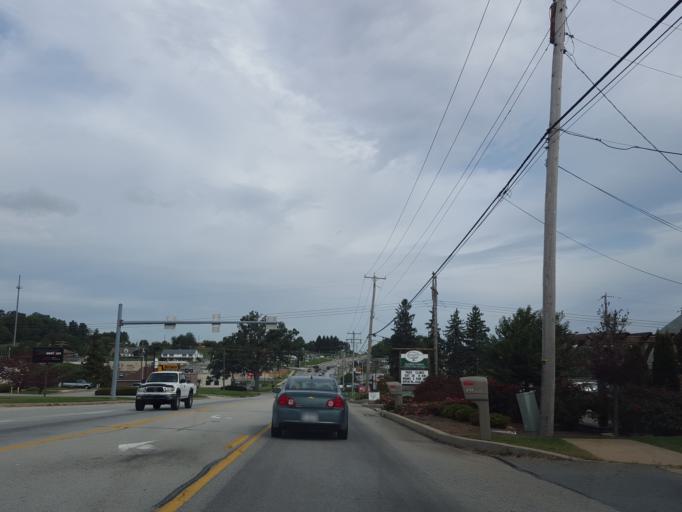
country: US
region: Pennsylvania
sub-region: York County
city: Spry
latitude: 39.9079
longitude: -76.6804
